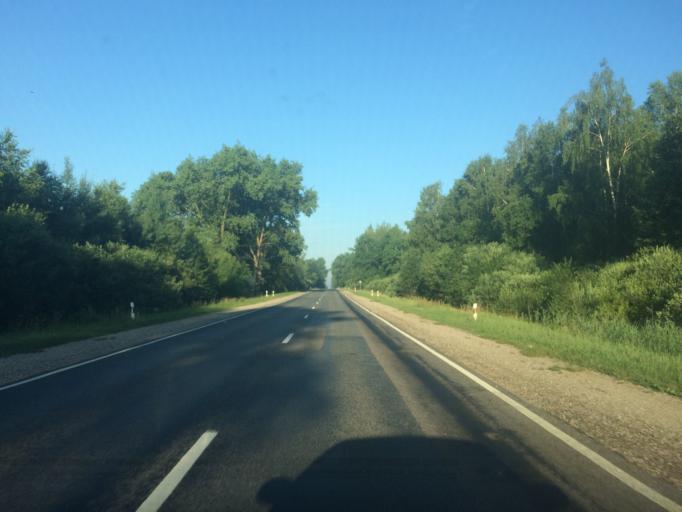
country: LT
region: Utenos apskritis
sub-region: Anyksciai
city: Anyksciai
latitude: 55.3560
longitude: 24.9658
